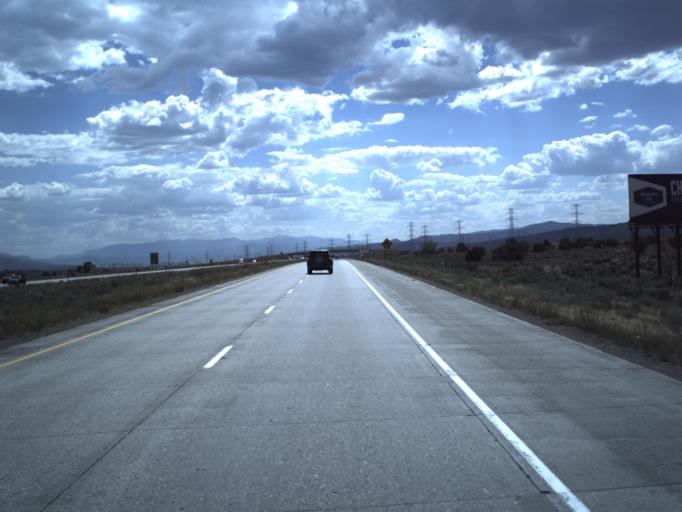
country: US
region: Utah
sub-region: Sevier County
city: Aurora
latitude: 38.8676
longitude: -111.9765
